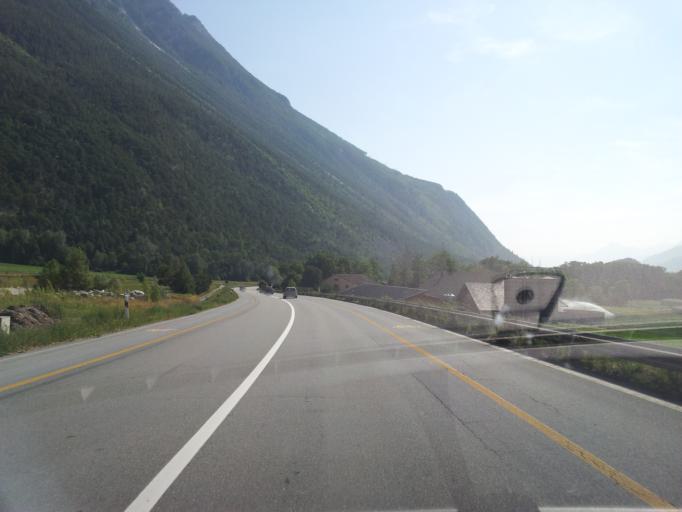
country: CH
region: Valais
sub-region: Leuk District
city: Varen
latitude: 46.3025
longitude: 7.6045
